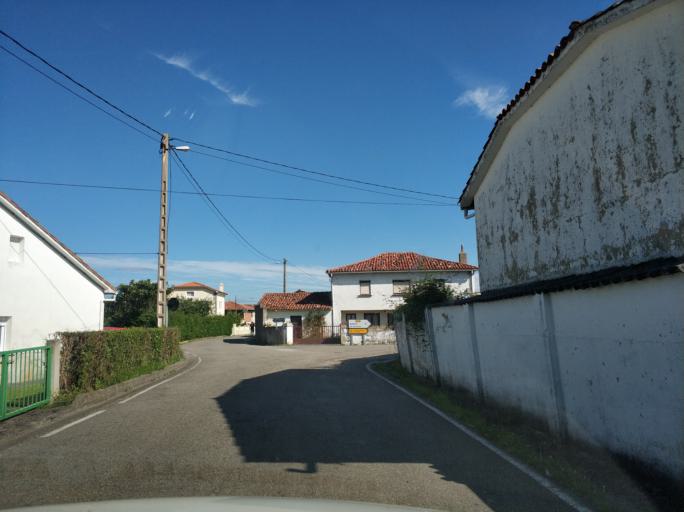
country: ES
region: Asturias
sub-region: Province of Asturias
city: Cudillero
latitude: 43.5770
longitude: -6.2387
